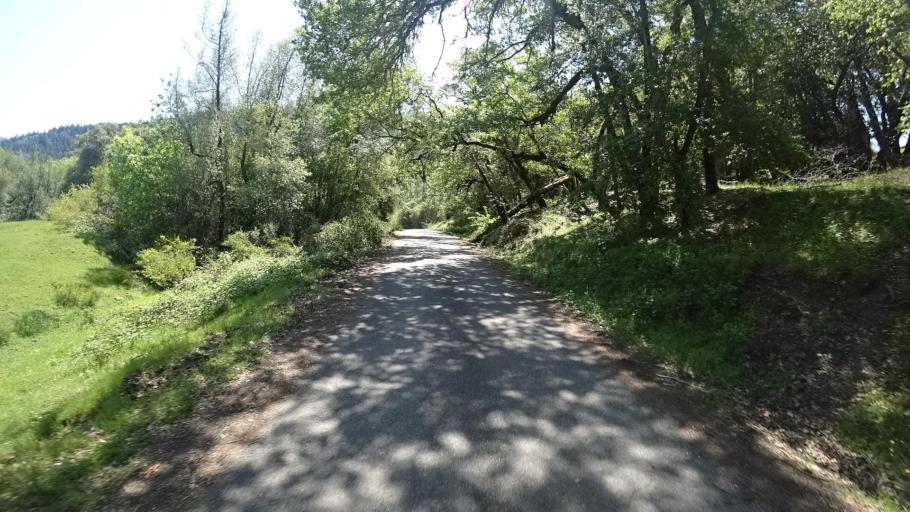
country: US
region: California
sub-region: Humboldt County
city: Redway
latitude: 40.1930
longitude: -123.5678
